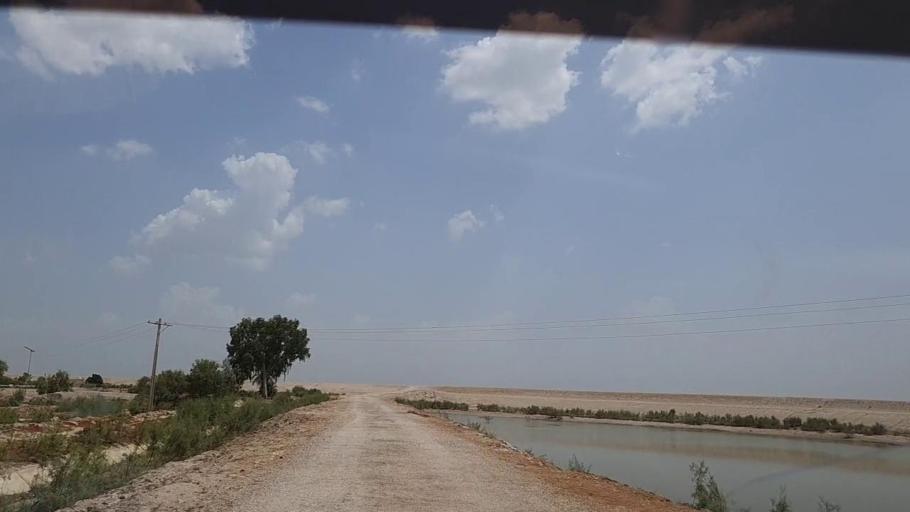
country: PK
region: Sindh
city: Bhan
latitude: 26.5026
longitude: 67.6403
